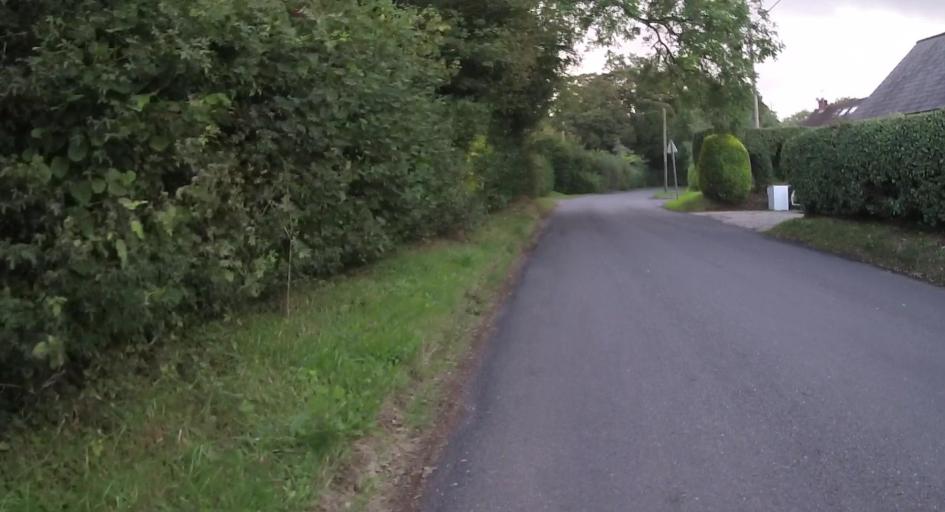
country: GB
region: England
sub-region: Hampshire
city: Four Marks
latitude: 51.1601
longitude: -1.0455
